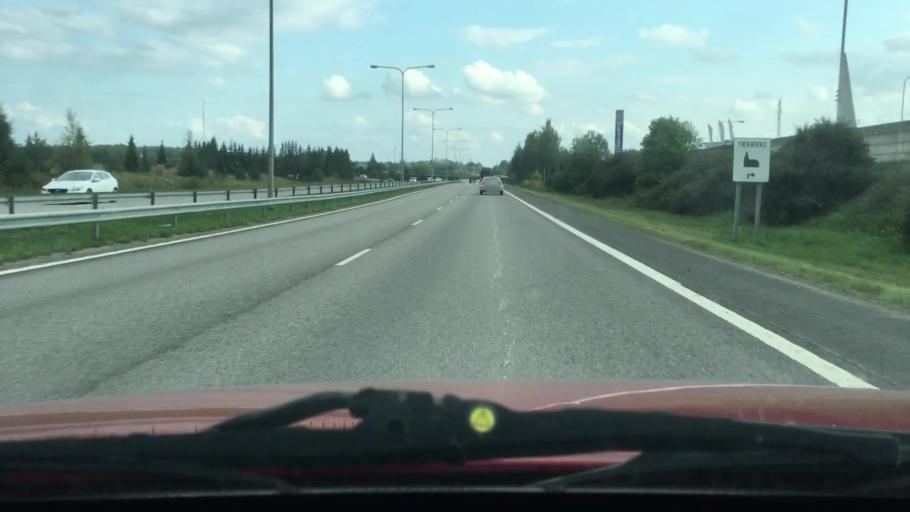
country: FI
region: Varsinais-Suomi
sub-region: Turku
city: Raisio
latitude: 60.4923
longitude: 22.1692
